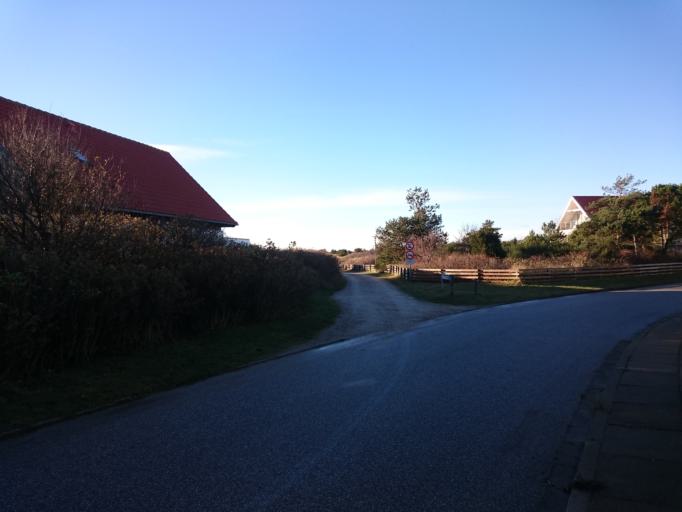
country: DK
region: North Denmark
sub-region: Frederikshavn Kommune
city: Skagen
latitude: 57.7161
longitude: 10.5672
